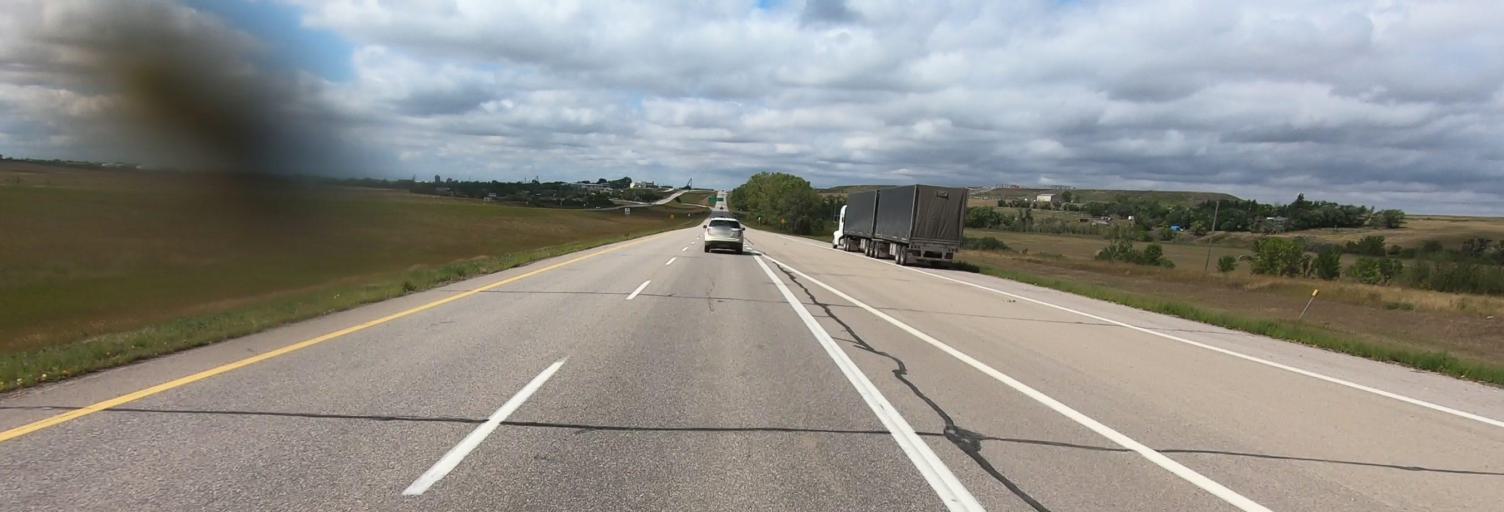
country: CA
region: Saskatchewan
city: Moose Jaw
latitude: 50.3939
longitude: -105.4692
